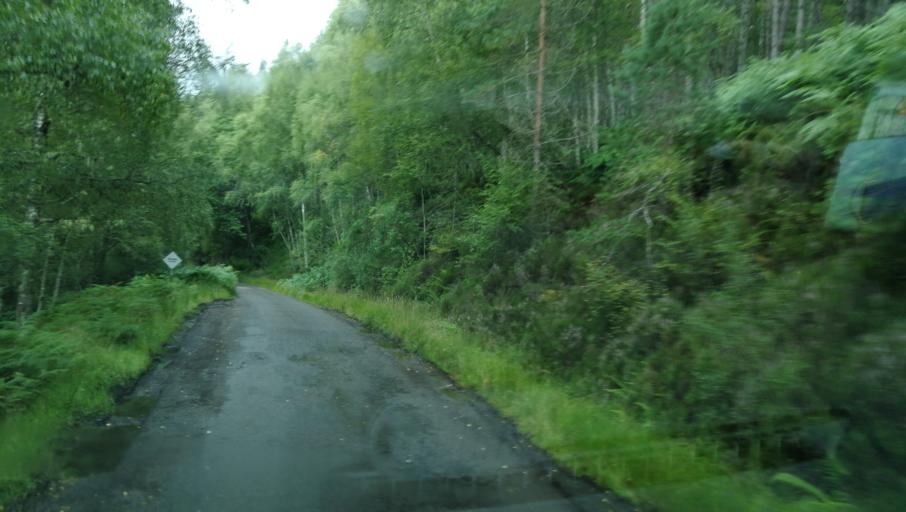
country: GB
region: Scotland
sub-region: Highland
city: Spean Bridge
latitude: 57.3015
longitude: -4.8914
